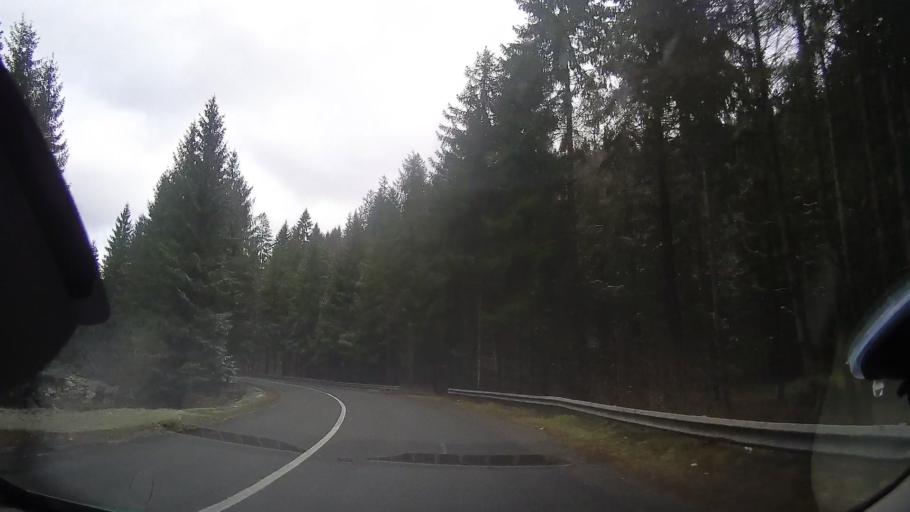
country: RO
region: Cluj
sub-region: Comuna Calatele
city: Calatele
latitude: 46.7483
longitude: 23.0147
